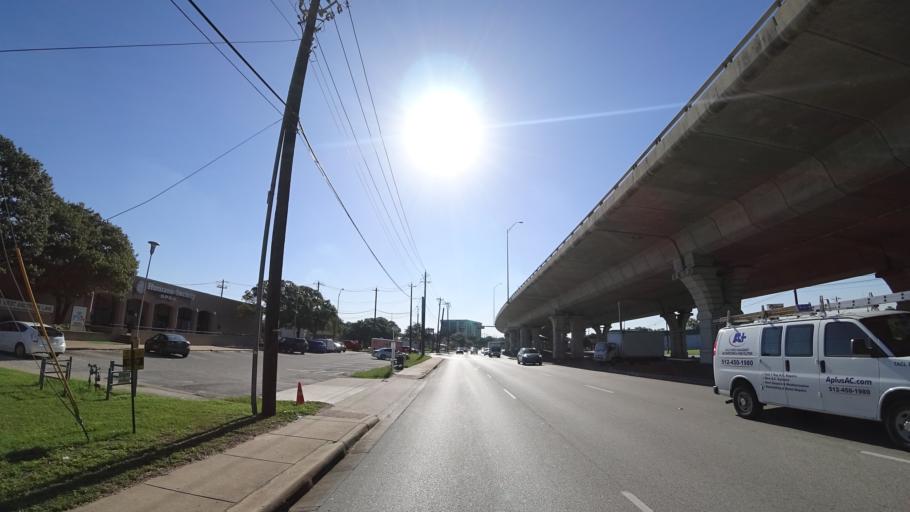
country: US
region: Texas
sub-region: Travis County
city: Austin
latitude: 30.3445
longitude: -97.7058
